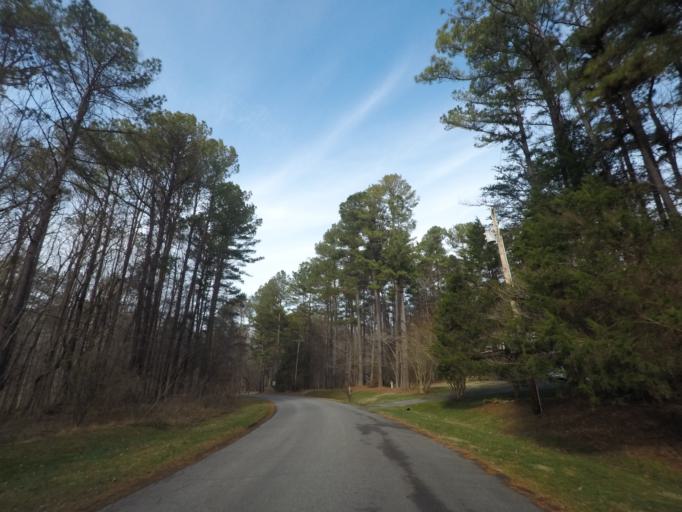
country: US
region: North Carolina
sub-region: Durham County
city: Durham
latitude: 36.0821
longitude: -78.9664
